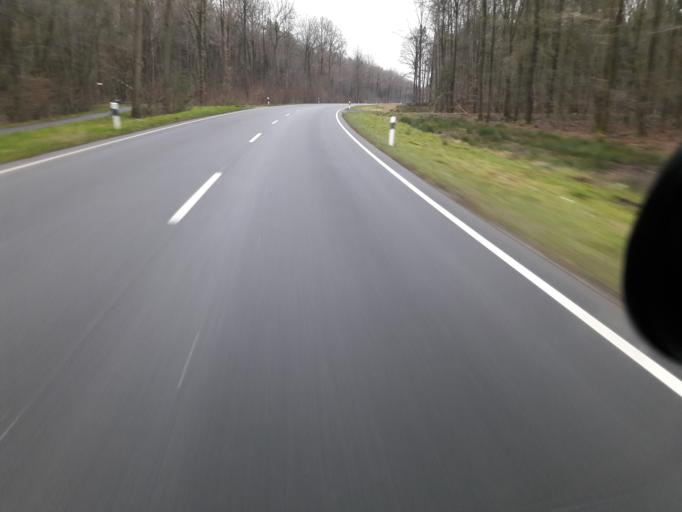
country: DE
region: Lower Saxony
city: Bad Bentheim
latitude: 52.3323
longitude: 7.1541
